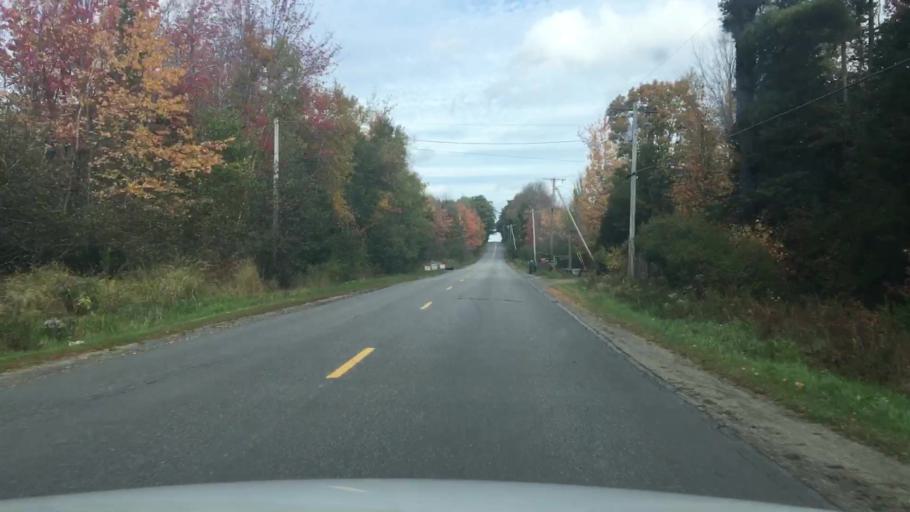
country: US
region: Maine
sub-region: Waldo County
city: Searsmont
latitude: 44.3870
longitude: -69.1330
